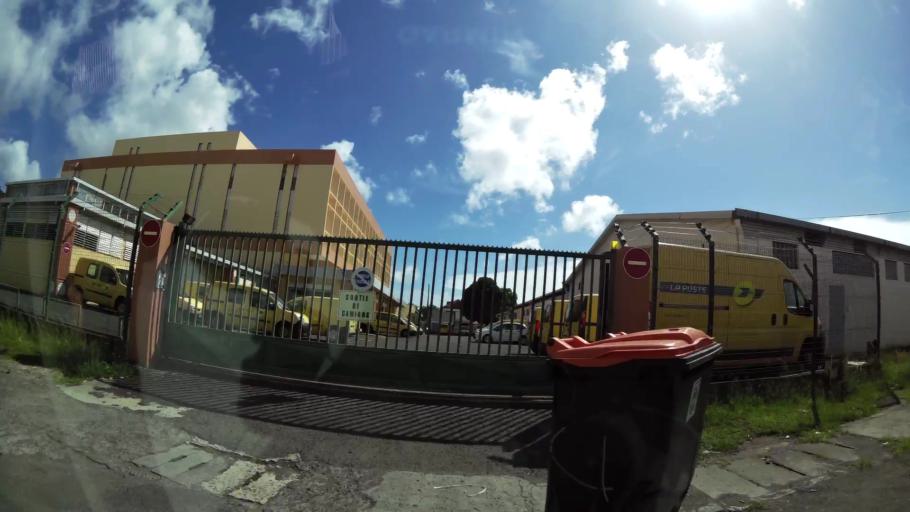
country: GP
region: Guadeloupe
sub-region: Guadeloupe
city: Pointe-a-Pitre
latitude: 16.2472
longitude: -61.5400
